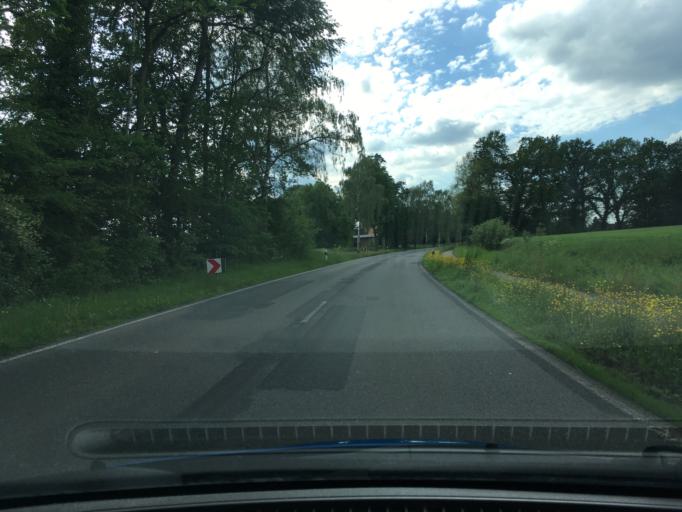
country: DE
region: Lower Saxony
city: Otter
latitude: 53.2571
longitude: 9.7450
